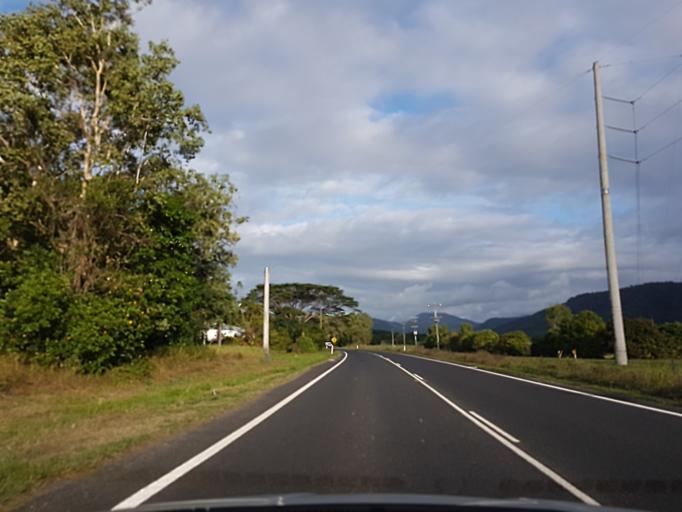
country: AU
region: Queensland
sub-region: Cairns
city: Port Douglas
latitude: -16.5198
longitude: 145.4499
